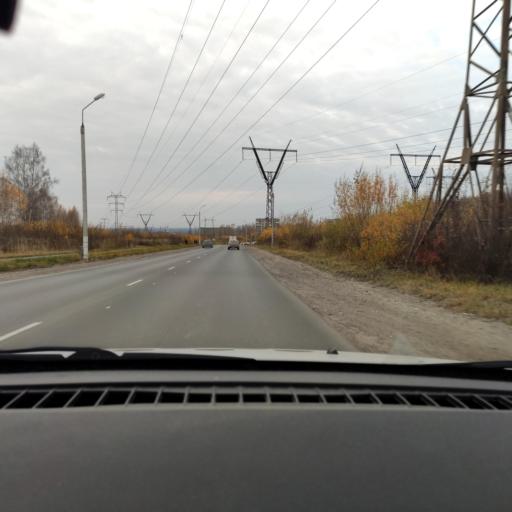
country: RU
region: Perm
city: Perm
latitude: 58.0982
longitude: 56.3947
